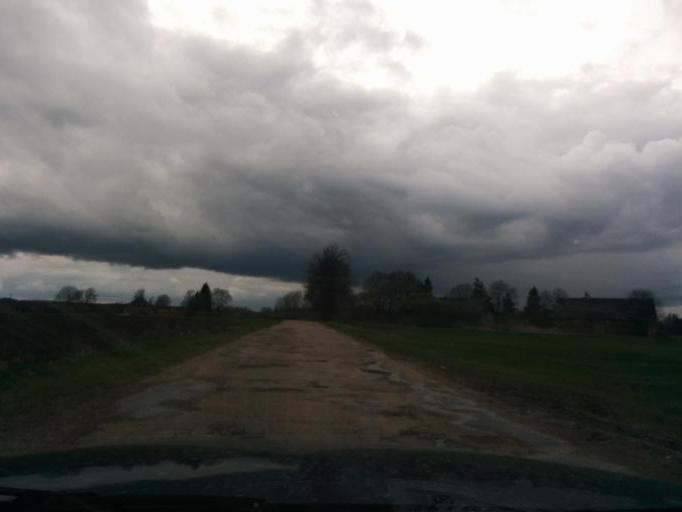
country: LV
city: Tervete
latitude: 56.3646
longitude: 23.5065
